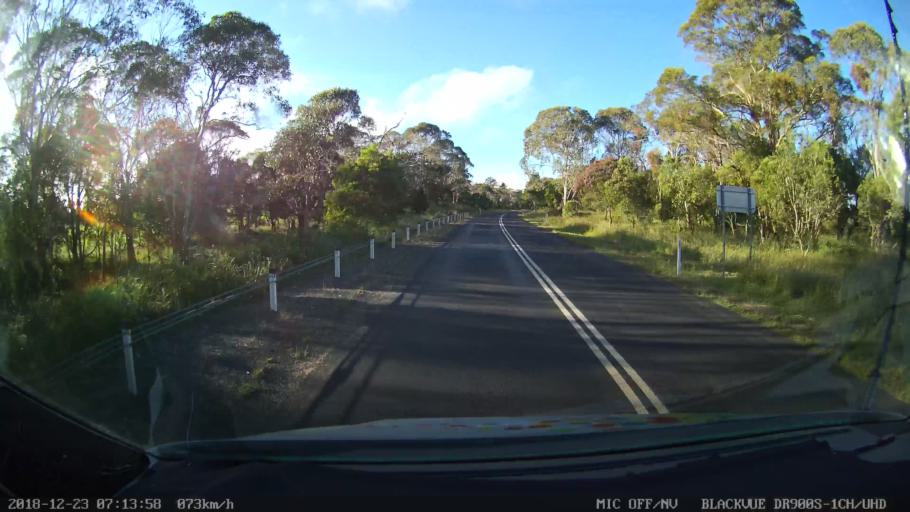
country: AU
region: New South Wales
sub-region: Bellingen
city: Dorrigo
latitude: -30.4300
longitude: 152.3247
